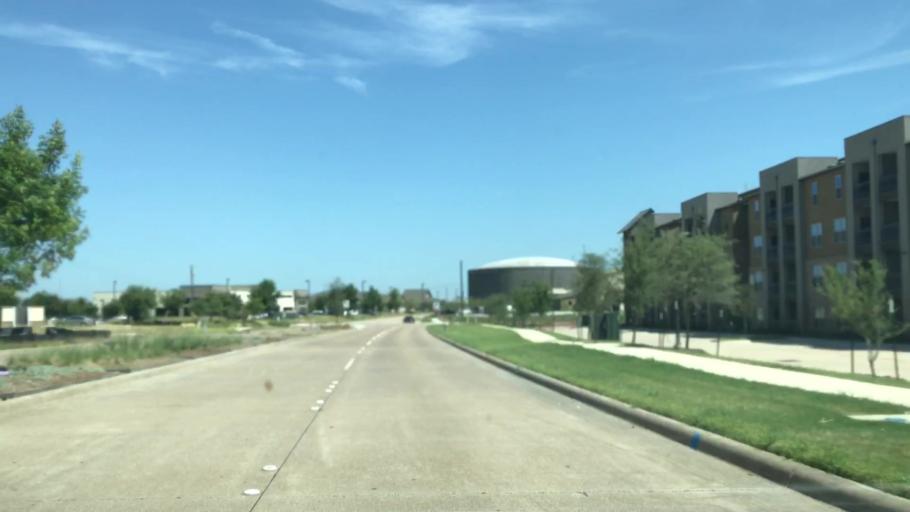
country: US
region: Texas
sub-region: Collin County
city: Allen
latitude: 33.1097
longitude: -96.6785
